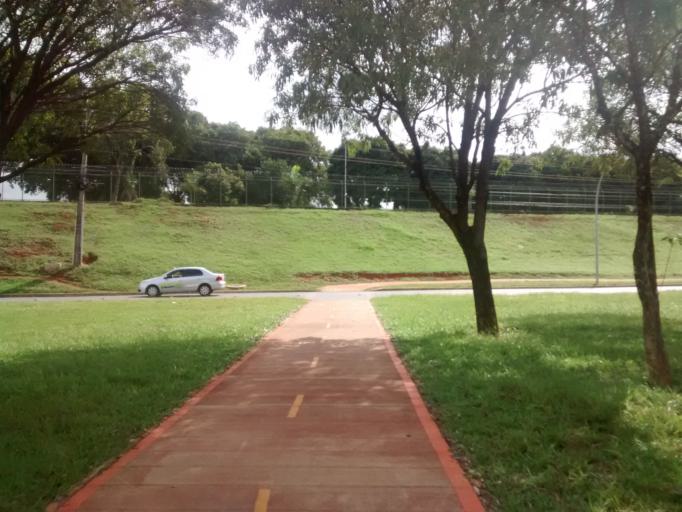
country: BR
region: Federal District
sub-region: Brasilia
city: Brasilia
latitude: -15.7829
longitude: -47.8907
